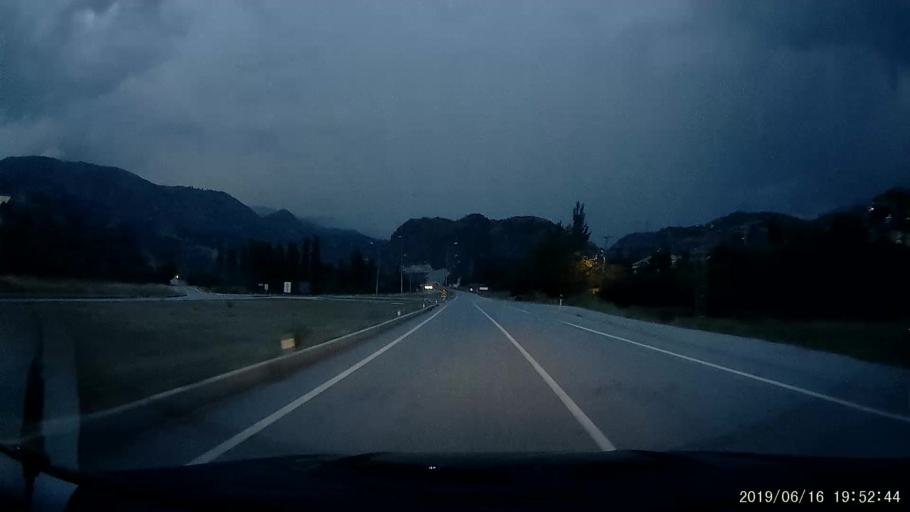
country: TR
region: Sivas
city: Koyulhisar
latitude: 40.2891
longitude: 37.7987
